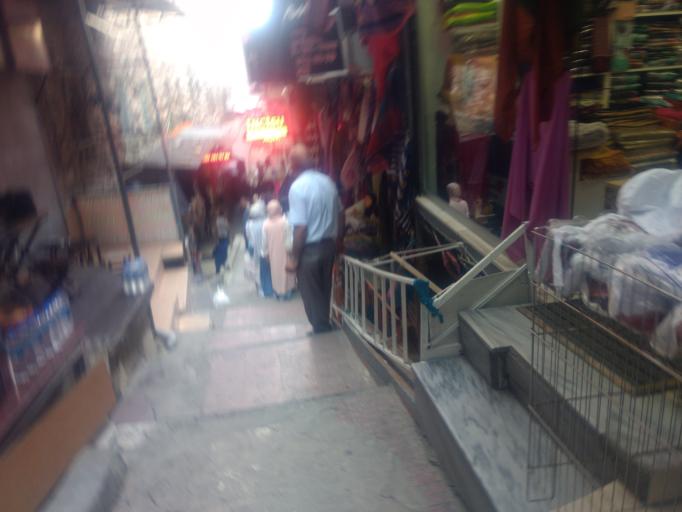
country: TR
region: Istanbul
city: Eminoenue
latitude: 41.0126
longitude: 28.9697
